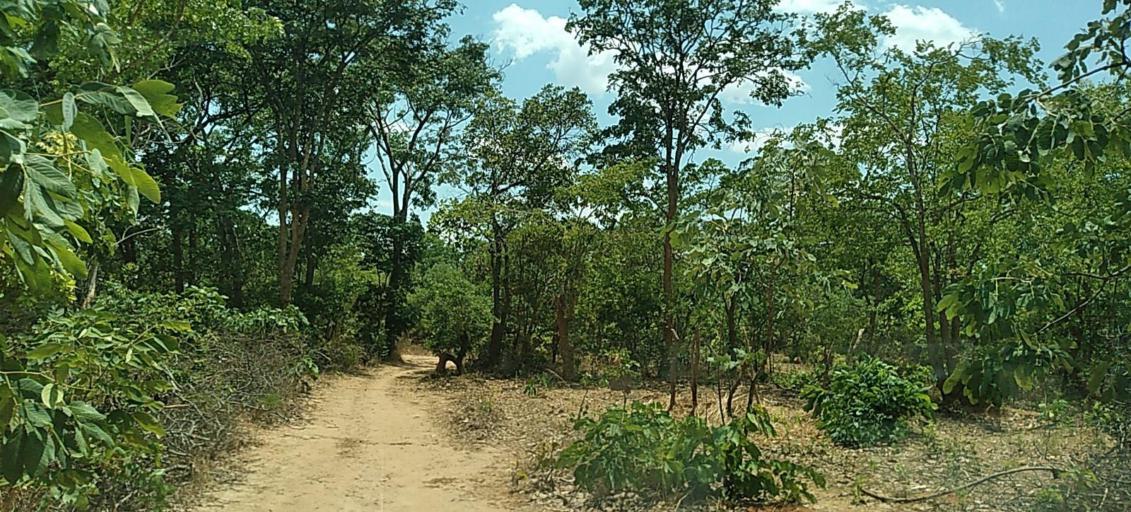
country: ZM
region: Central
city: Kapiri Mposhi
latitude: -13.6290
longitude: 28.7768
